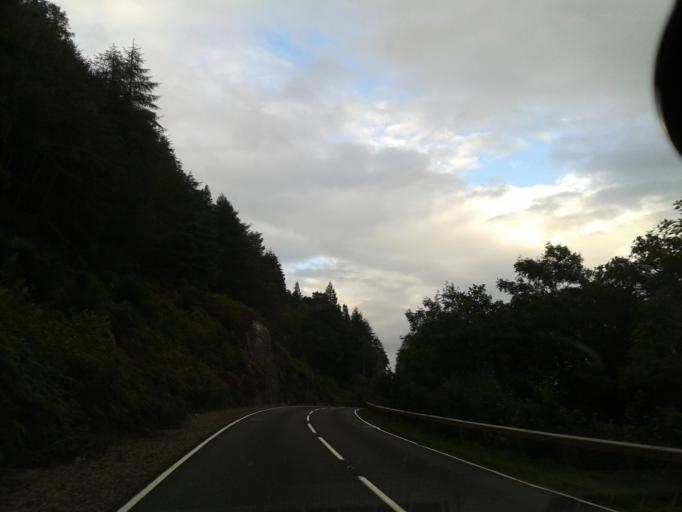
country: GB
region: Scotland
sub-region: Highland
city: Beauly
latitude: 57.3463
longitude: -4.4183
